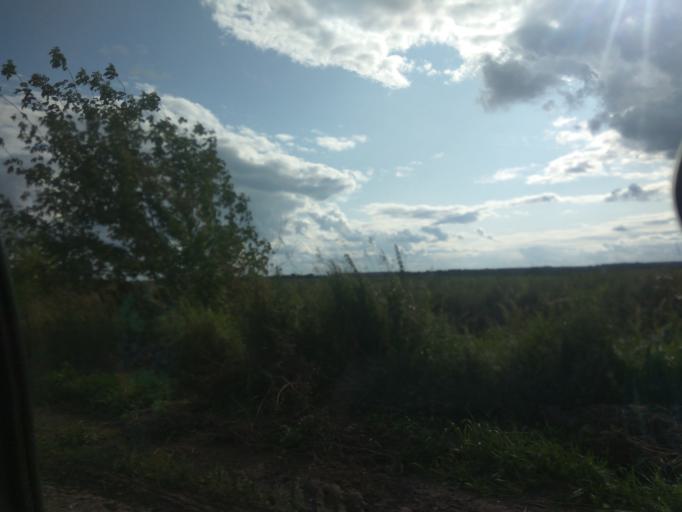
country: RU
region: Moskovskaya
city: Ramenskoye
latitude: 55.5034
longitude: 38.2261
